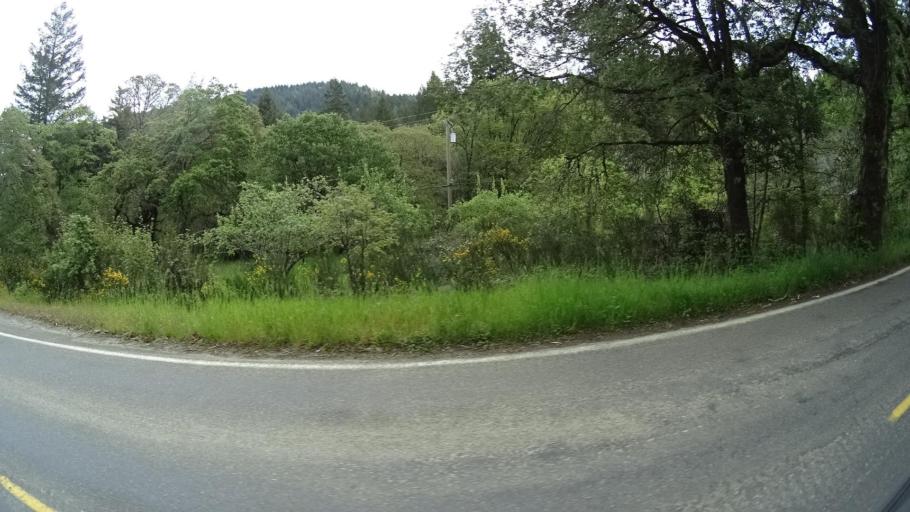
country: US
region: California
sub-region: Humboldt County
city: Redway
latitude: 40.1121
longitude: -123.8905
